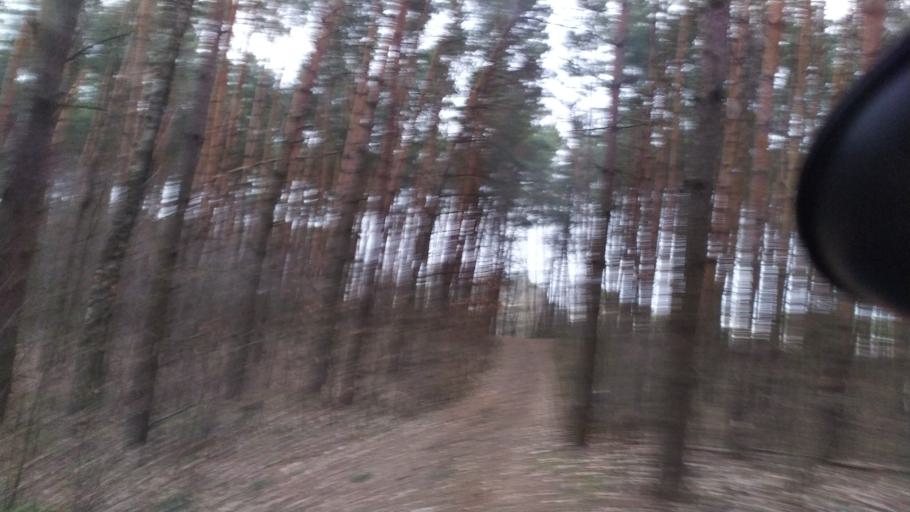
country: PL
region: Lublin Voivodeship
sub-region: Powiat lubartowski
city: Abramow
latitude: 51.4278
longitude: 22.2925
